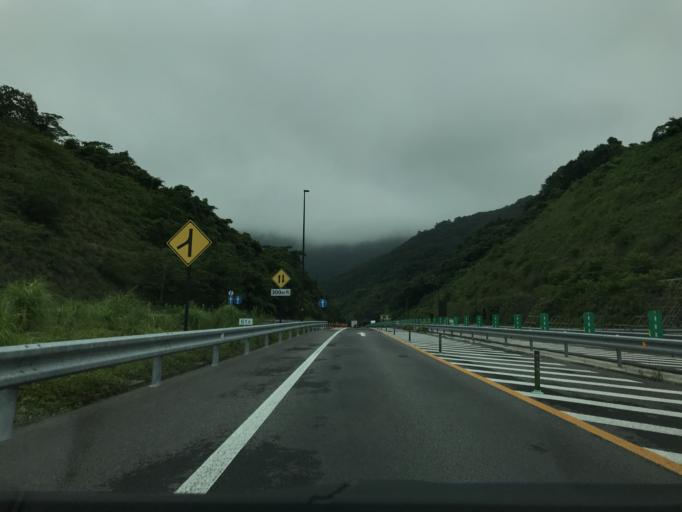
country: JP
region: Oita
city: Bungo-Takada-shi
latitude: 33.4967
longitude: 131.3181
